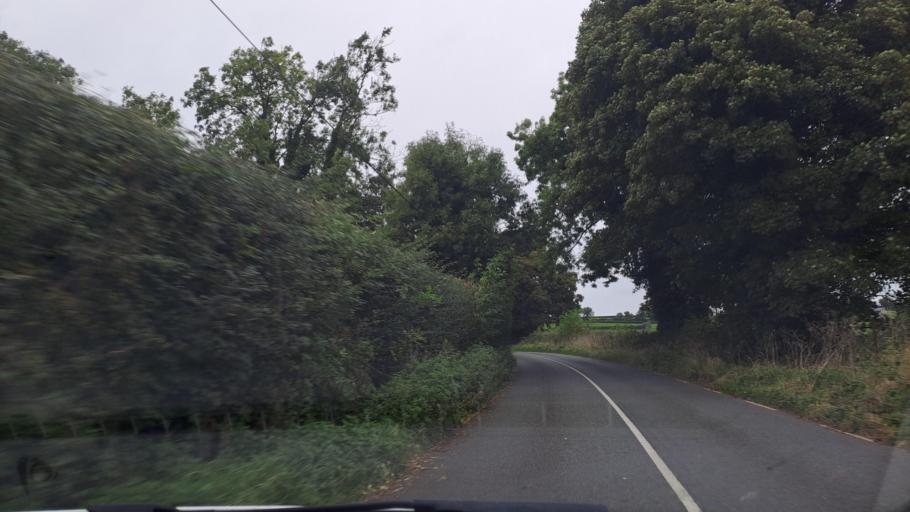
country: IE
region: Ulster
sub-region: County Monaghan
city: Carrickmacross
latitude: 53.9483
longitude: -6.6755
